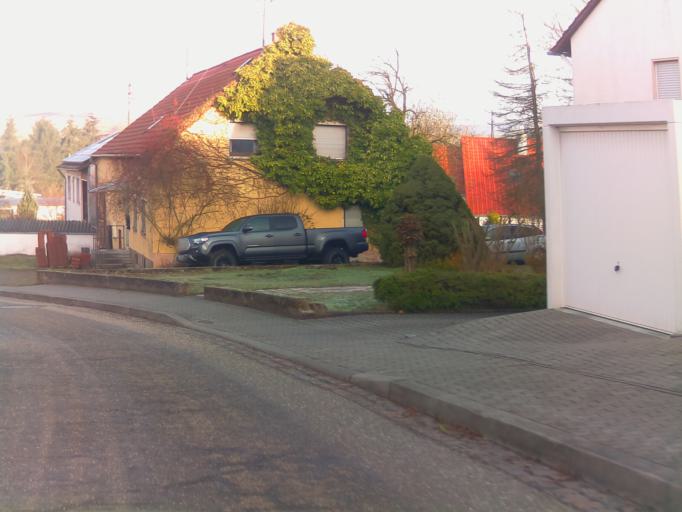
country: DE
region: Rheinland-Pfalz
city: Bruchmuhlbach-Miesau
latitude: 49.4159
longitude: 7.4339
